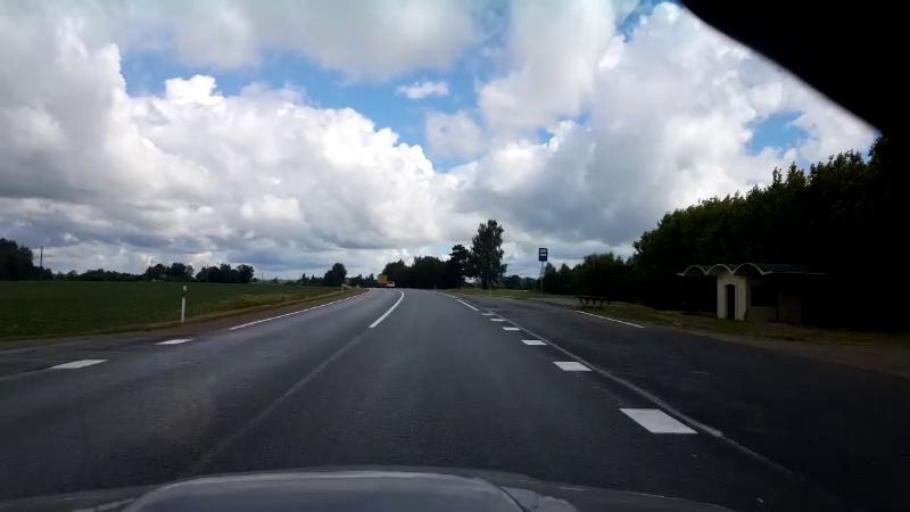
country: LV
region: Bauskas Rajons
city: Bauska
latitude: 56.4884
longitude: 24.1771
